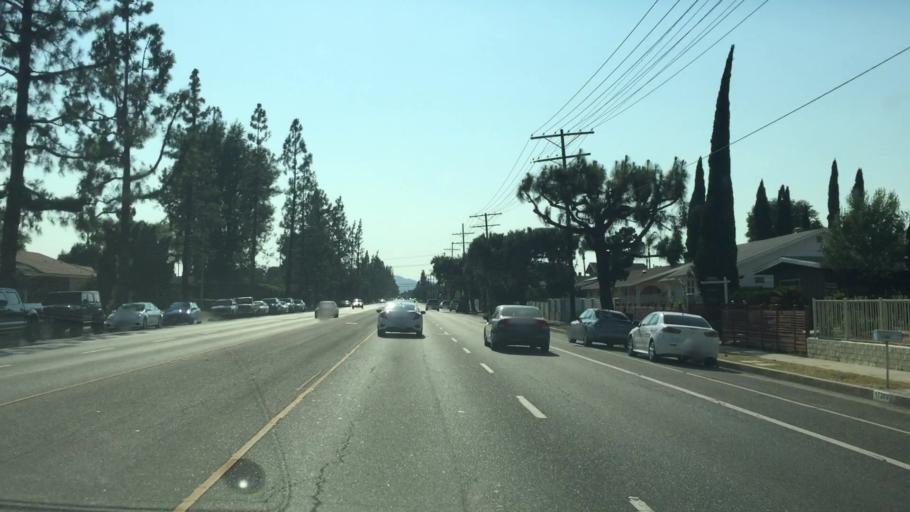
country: US
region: California
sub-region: Los Angeles County
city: Northridge
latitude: 34.2576
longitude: -118.5083
